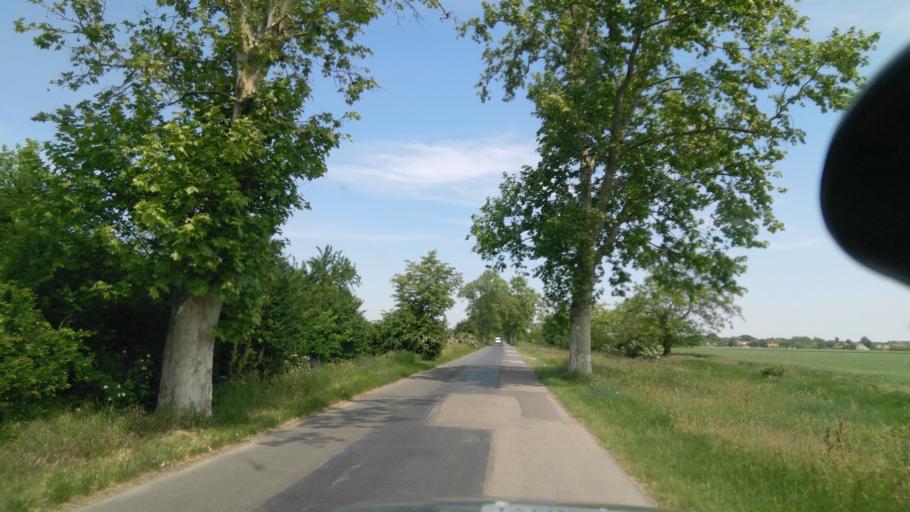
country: HU
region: Csongrad
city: Szekkutas
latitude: 46.5781
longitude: 20.4662
